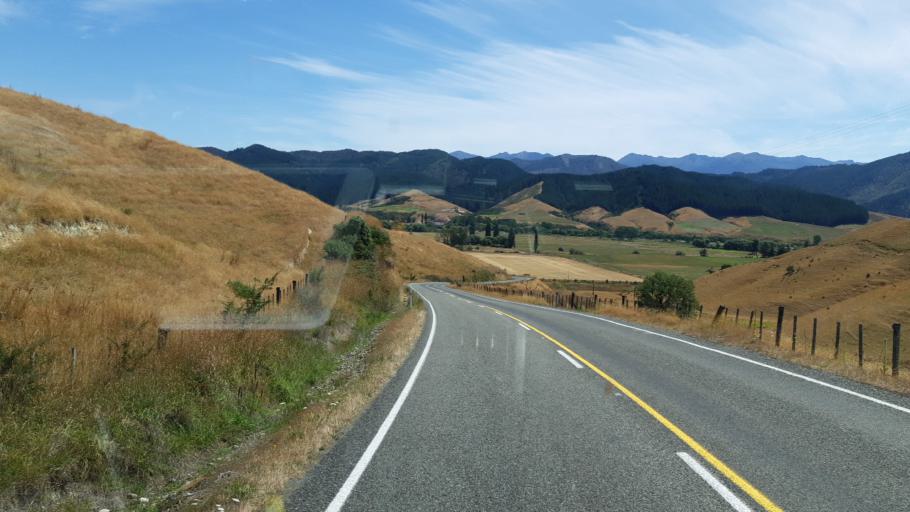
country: NZ
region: Tasman
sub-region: Tasman District
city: Wakefield
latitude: -41.3430
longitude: 172.8143
